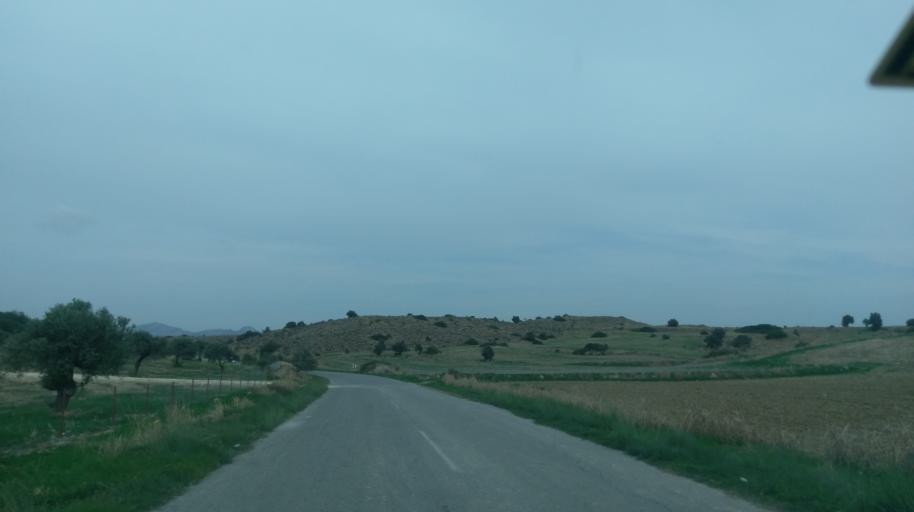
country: CY
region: Ammochostos
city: Trikomo
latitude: 35.3397
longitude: 33.9298
